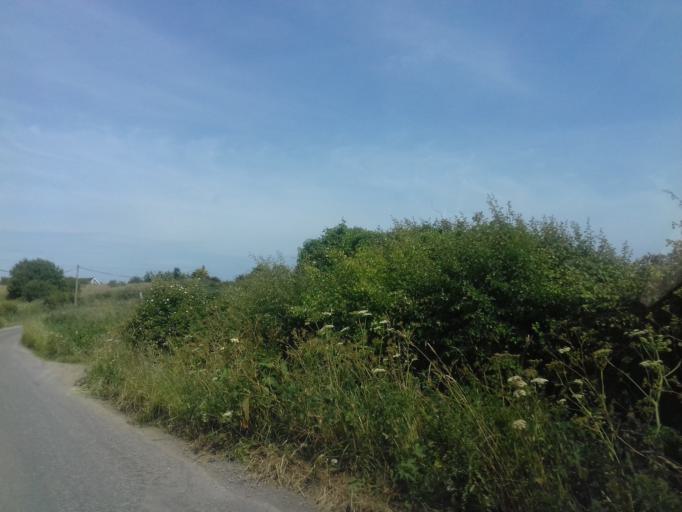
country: IE
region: Leinster
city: Lusk
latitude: 53.5284
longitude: -6.1450
